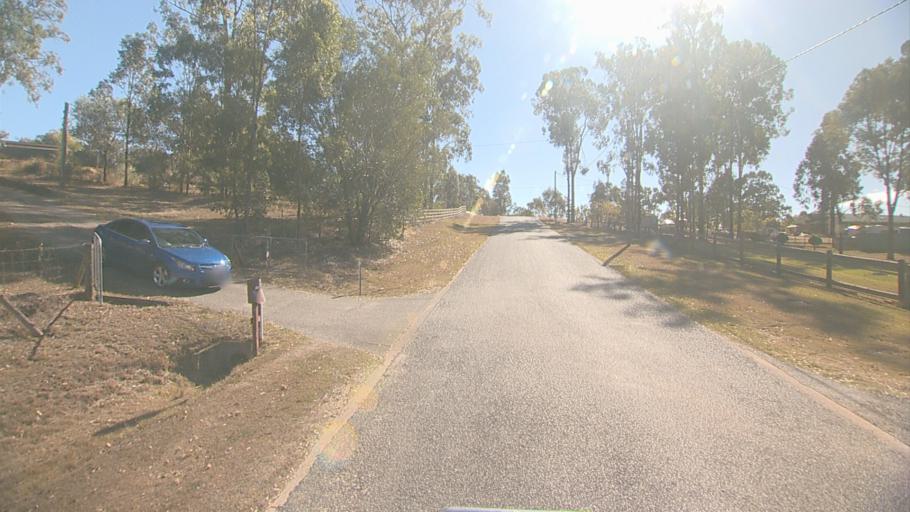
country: AU
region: Queensland
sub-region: Logan
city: Cedar Vale
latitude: -27.8834
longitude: 153.0037
